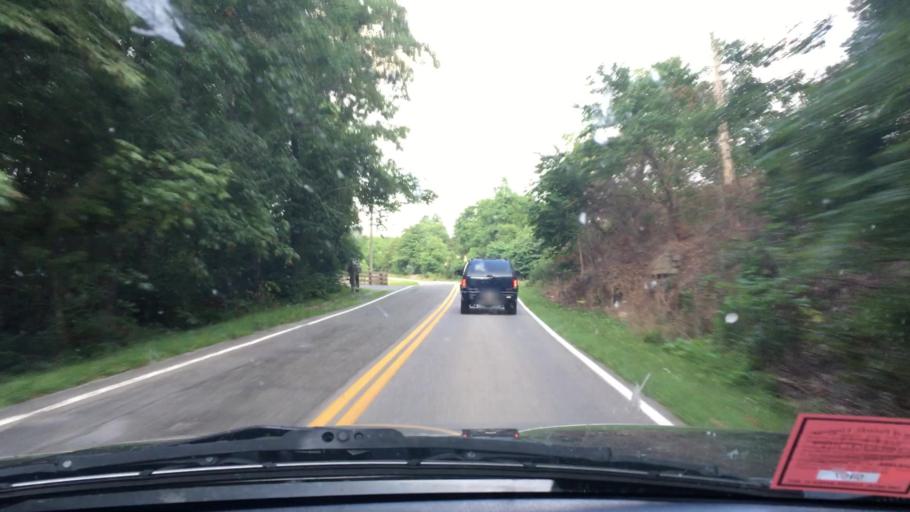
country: US
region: Virginia
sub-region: Pulaski County
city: Dublin
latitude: 37.0586
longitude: -80.7047
